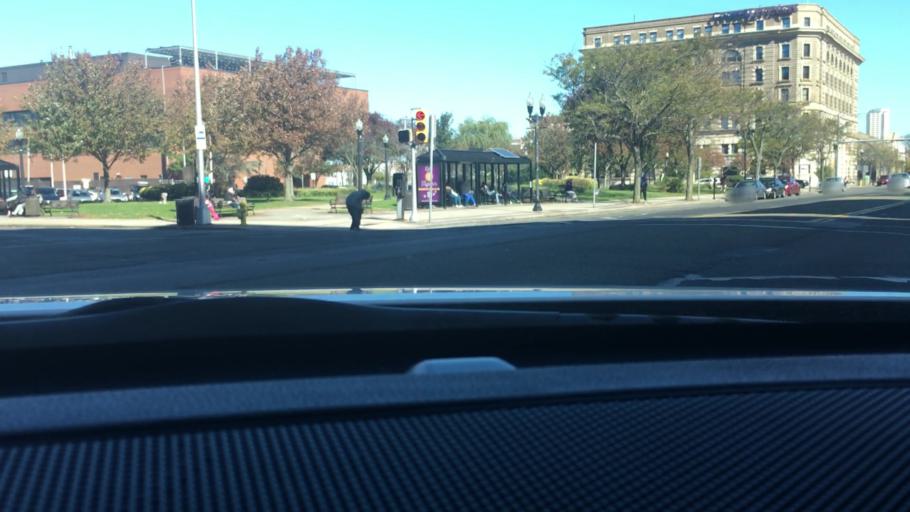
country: US
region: New Jersey
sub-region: Atlantic County
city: Atlantic City
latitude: 39.3625
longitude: -74.4269
